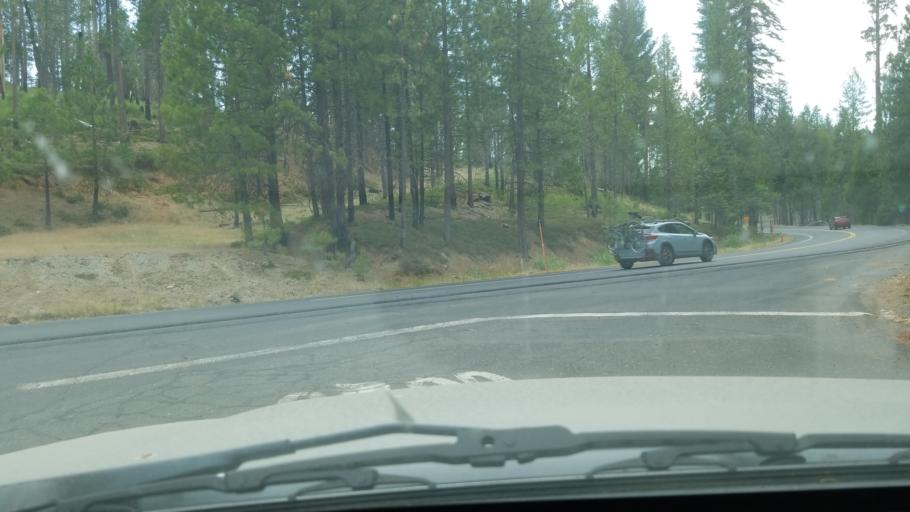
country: US
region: California
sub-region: Mariposa County
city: Midpines
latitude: 37.8151
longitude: -119.8750
